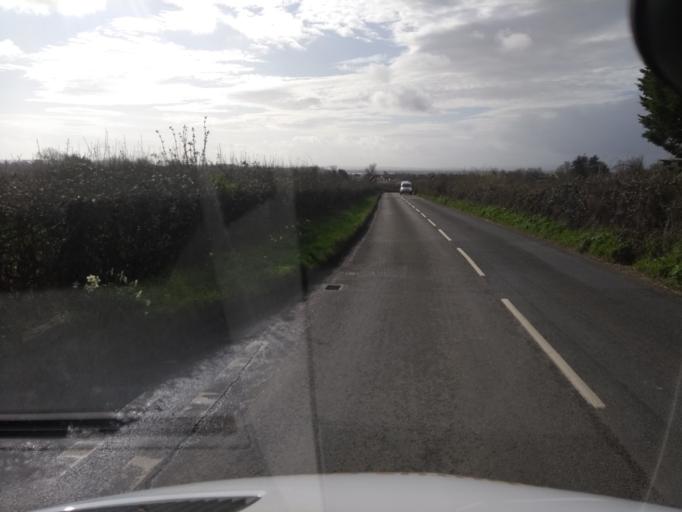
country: GB
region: England
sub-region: Somerset
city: Woolavington
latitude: 51.1618
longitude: -2.9349
